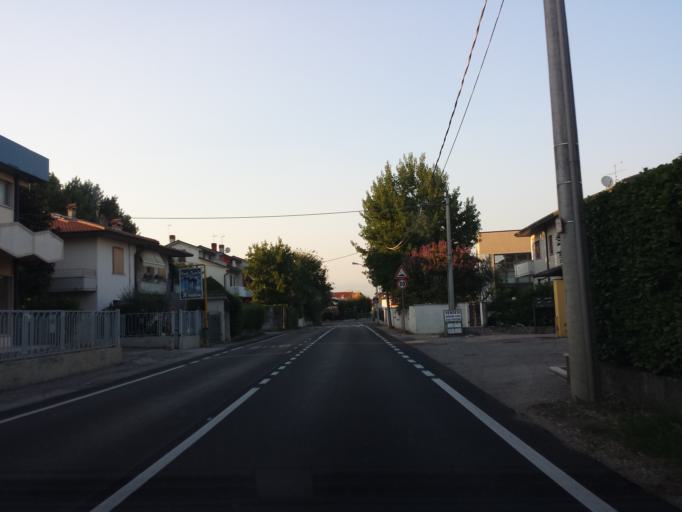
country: IT
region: Veneto
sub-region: Provincia di Vicenza
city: Monticello Conte Otto
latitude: 45.5763
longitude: 11.5605
